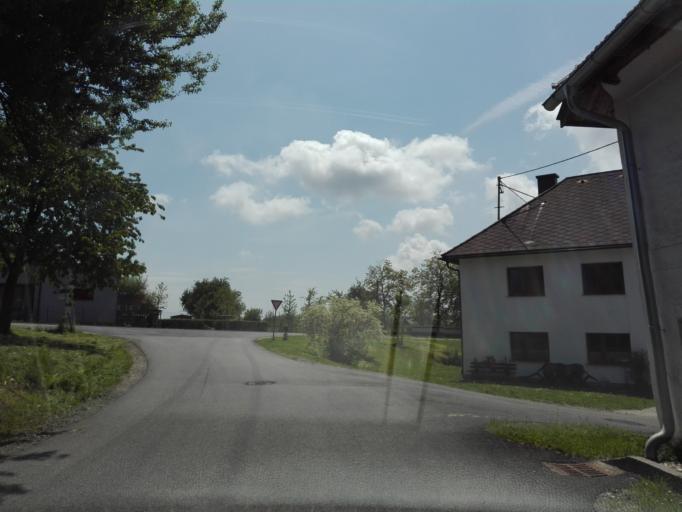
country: AT
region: Upper Austria
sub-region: Politischer Bezirk Rohrbach
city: Atzesberg
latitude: 48.4163
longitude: 13.9153
